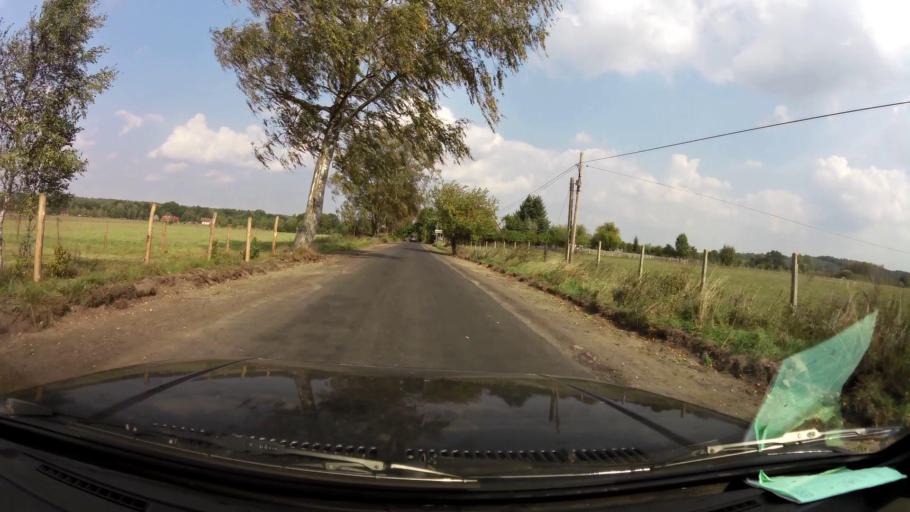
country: PL
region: West Pomeranian Voivodeship
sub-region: Powiat koszalinski
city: Bobolice
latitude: 54.1099
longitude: 16.5009
